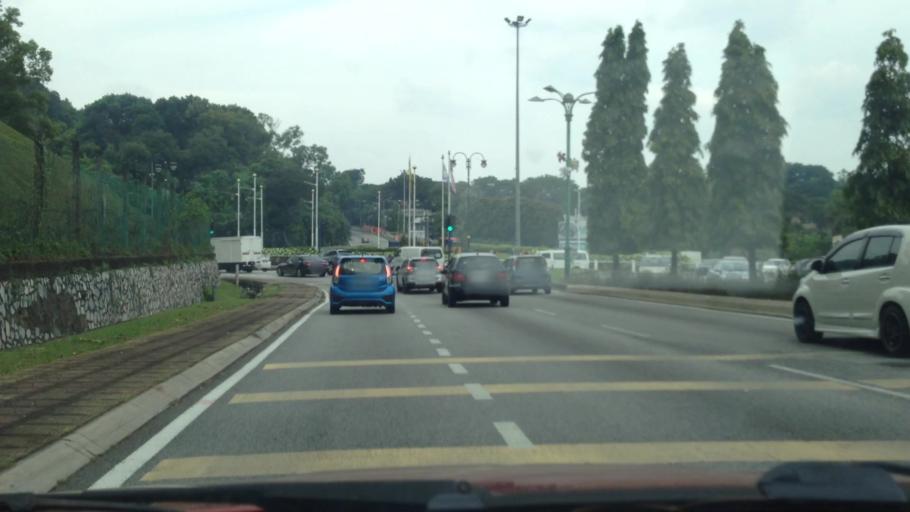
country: MY
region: Selangor
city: Shah Alam
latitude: 3.0753
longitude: 101.5338
